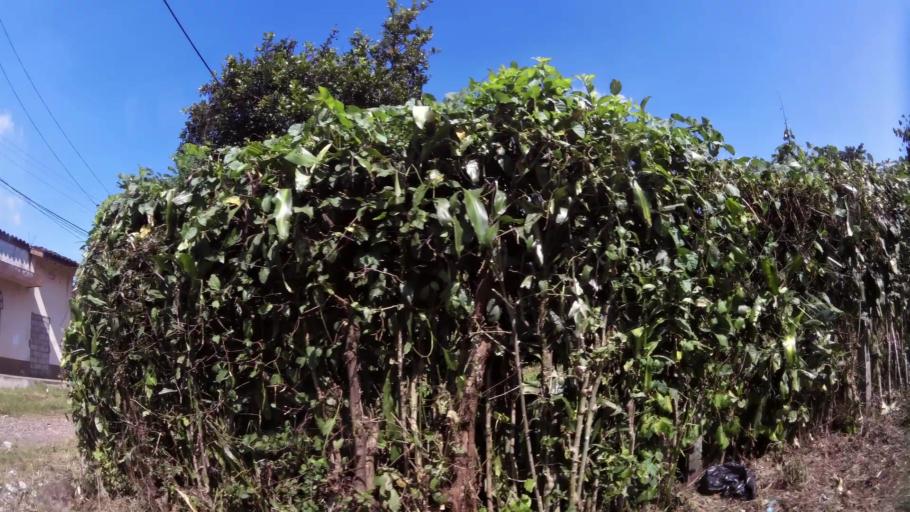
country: GT
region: Suchitepeque
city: Mazatenango
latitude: 14.5297
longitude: -91.4842
